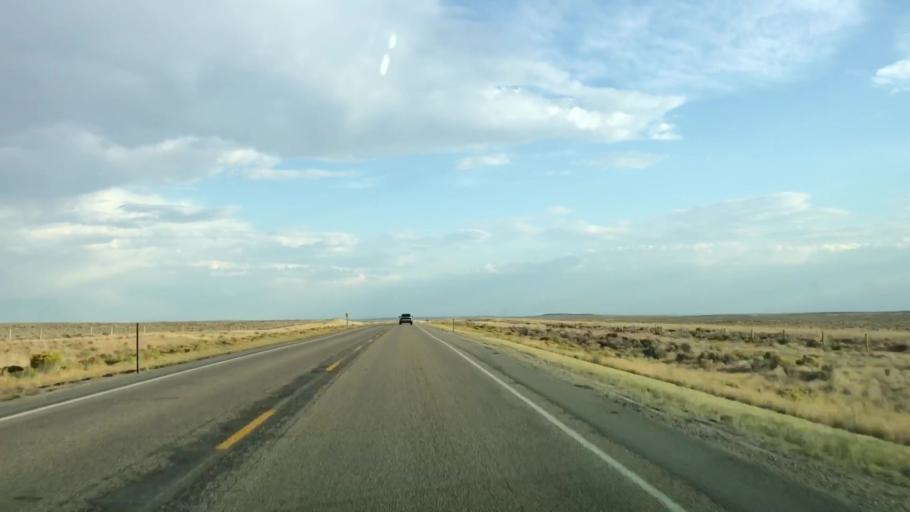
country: US
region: Wyoming
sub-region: Sublette County
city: Pinedale
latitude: 42.4086
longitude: -109.5511
